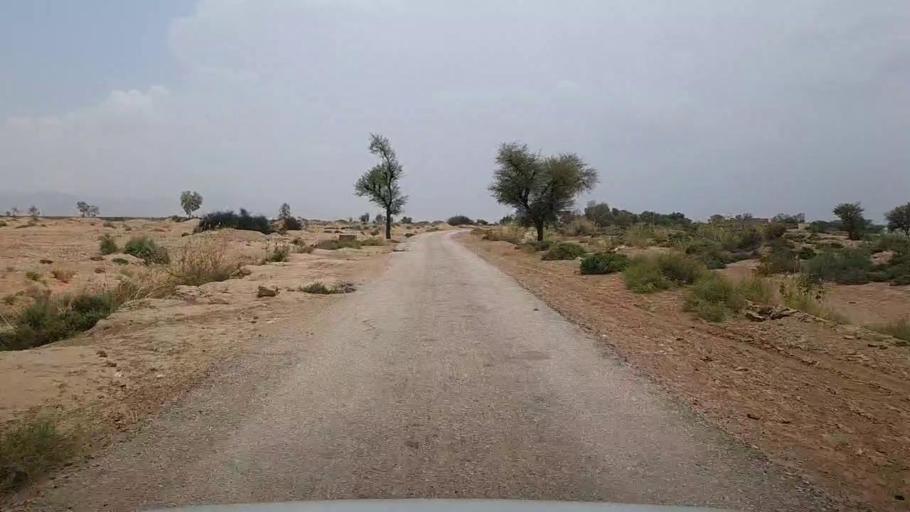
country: PK
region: Sindh
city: Sehwan
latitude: 26.3496
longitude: 67.7951
